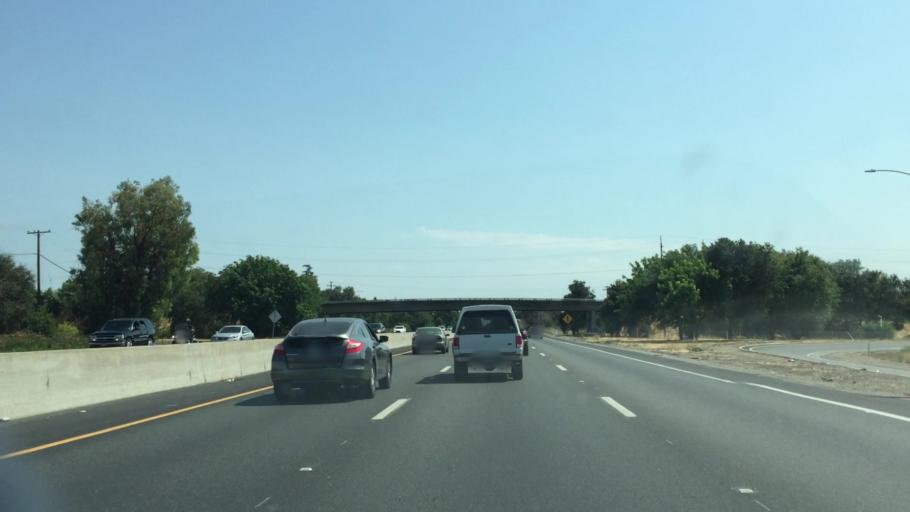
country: US
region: California
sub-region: San Joaquin County
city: Morada
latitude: 38.0388
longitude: -121.2585
